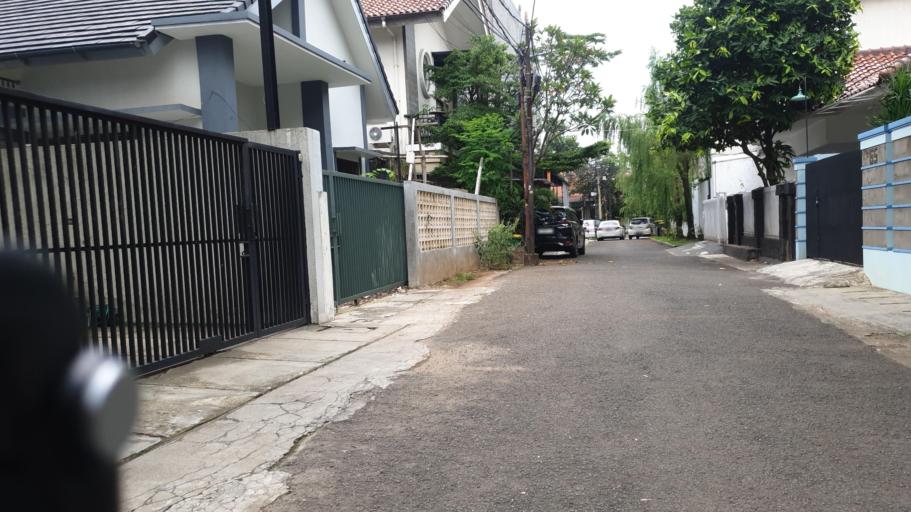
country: ID
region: Banten
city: South Tangerang
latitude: -6.2891
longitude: 106.7937
